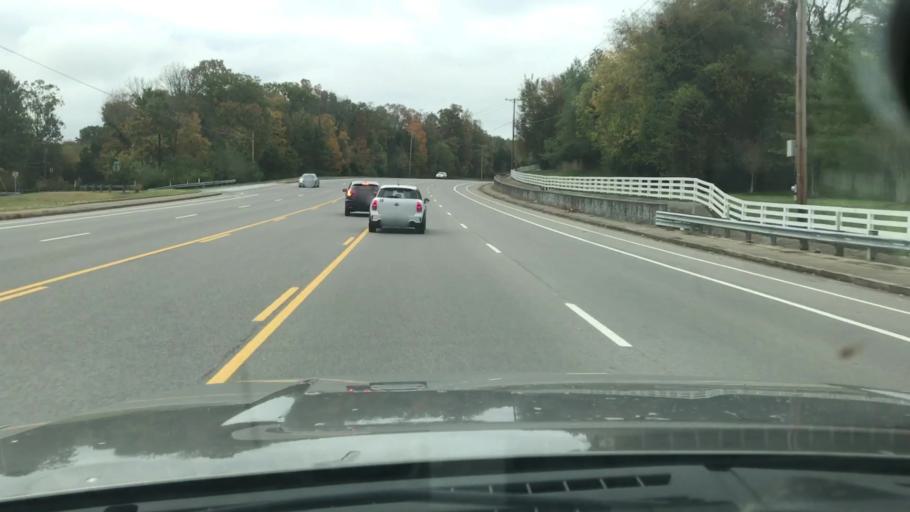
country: US
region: Tennessee
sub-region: Williamson County
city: Franklin
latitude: 35.9729
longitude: -86.8853
